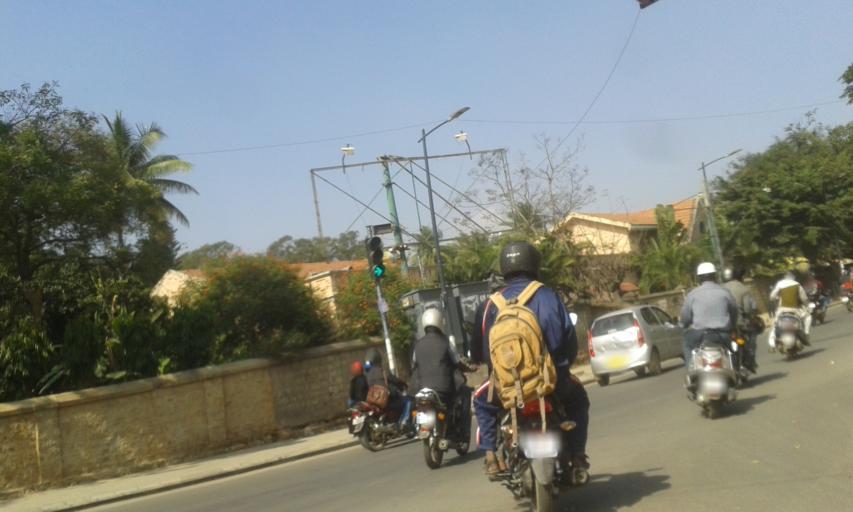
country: IN
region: Karnataka
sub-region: Bangalore Urban
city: Bangalore
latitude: 12.9682
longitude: 77.6063
